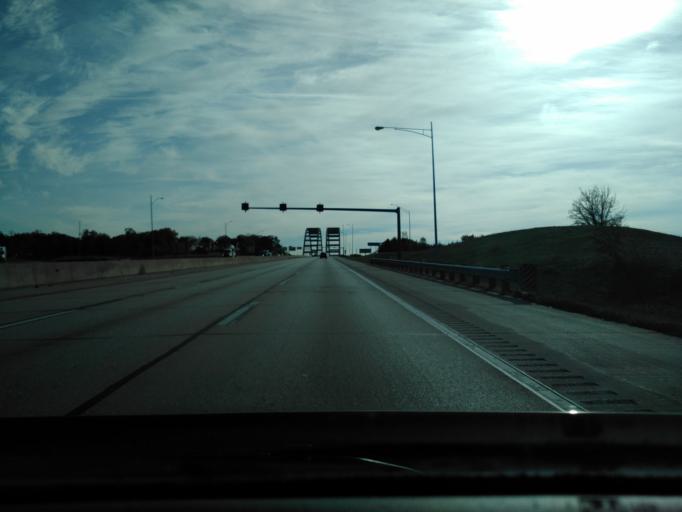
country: US
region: Missouri
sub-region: Saint Louis County
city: Oakville
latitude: 38.4899
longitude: -90.2872
